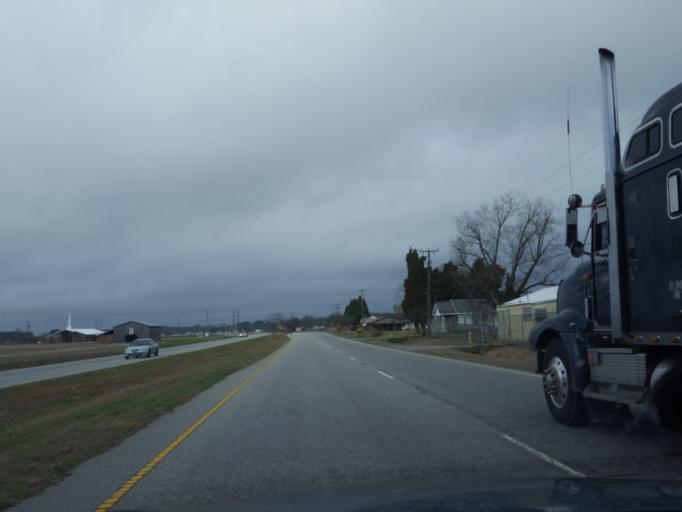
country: US
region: North Carolina
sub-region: Washington County
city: Plymouth
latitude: 35.8323
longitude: -76.8072
